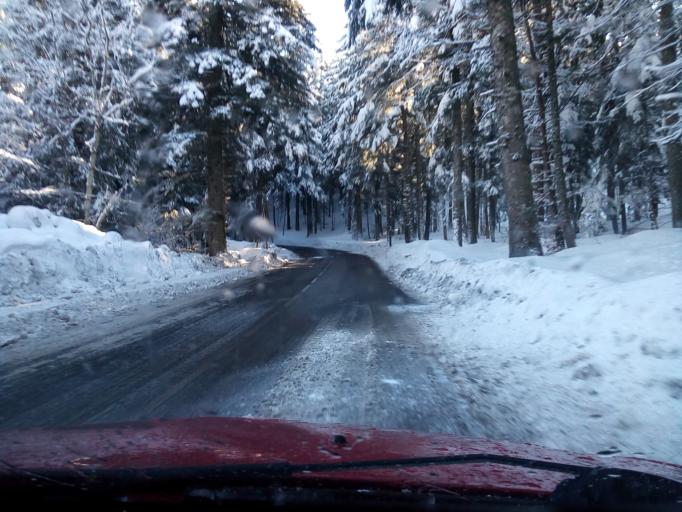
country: FR
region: Rhone-Alpes
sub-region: Departement de l'Isere
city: Le Sappey-en-Chartreuse
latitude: 45.3024
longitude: 5.7688
